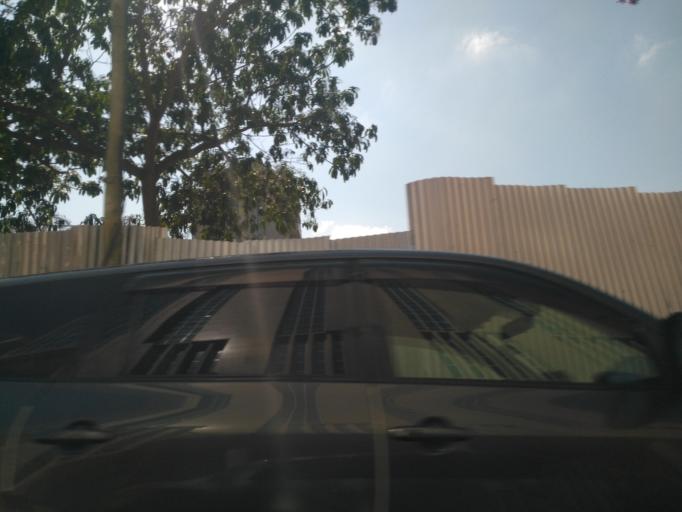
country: TZ
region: Arusha
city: Arusha
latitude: -3.3703
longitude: 36.6941
